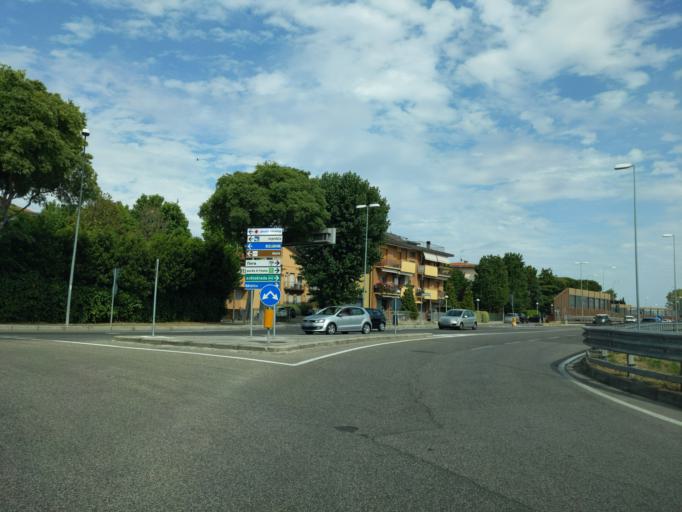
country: IT
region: Emilia-Romagna
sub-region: Provincia di Rimini
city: Rivazzurra
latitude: 44.0418
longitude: 12.5898
